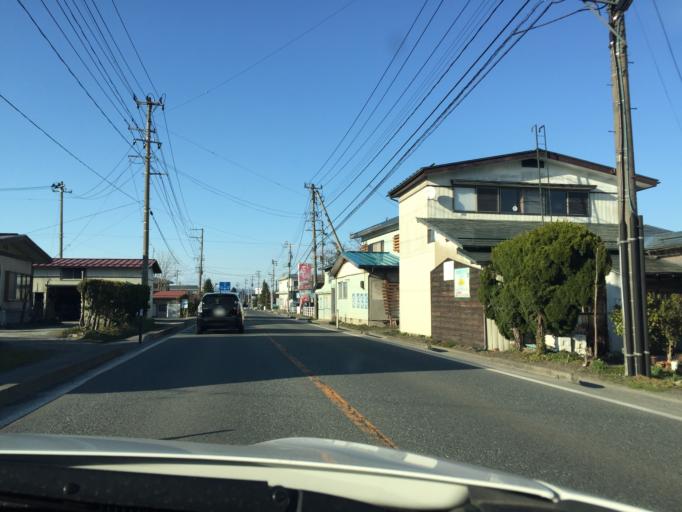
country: JP
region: Yamagata
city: Yonezawa
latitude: 37.9538
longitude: 140.1245
